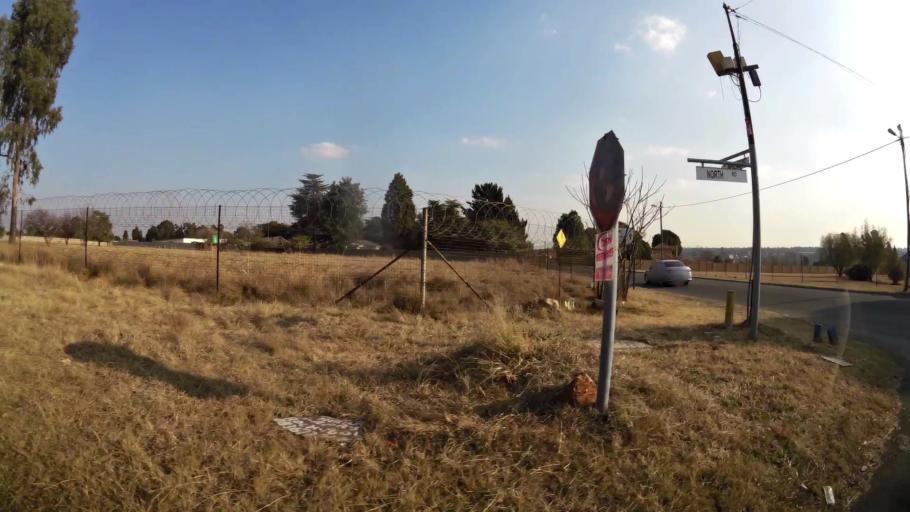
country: ZA
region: Gauteng
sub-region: Ekurhuleni Metropolitan Municipality
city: Benoni
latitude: -26.1373
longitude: 28.3625
